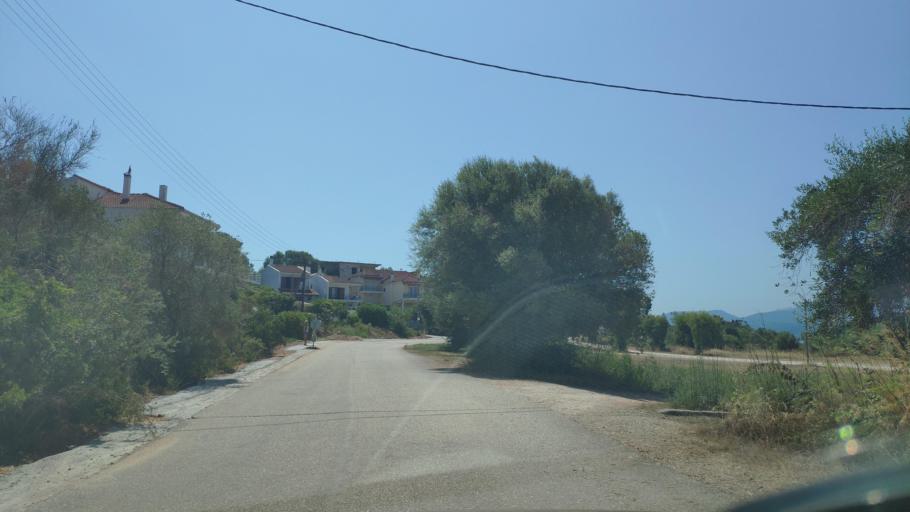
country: GR
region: Epirus
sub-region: Nomos Artas
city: Aneza
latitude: 39.0137
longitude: 20.9174
